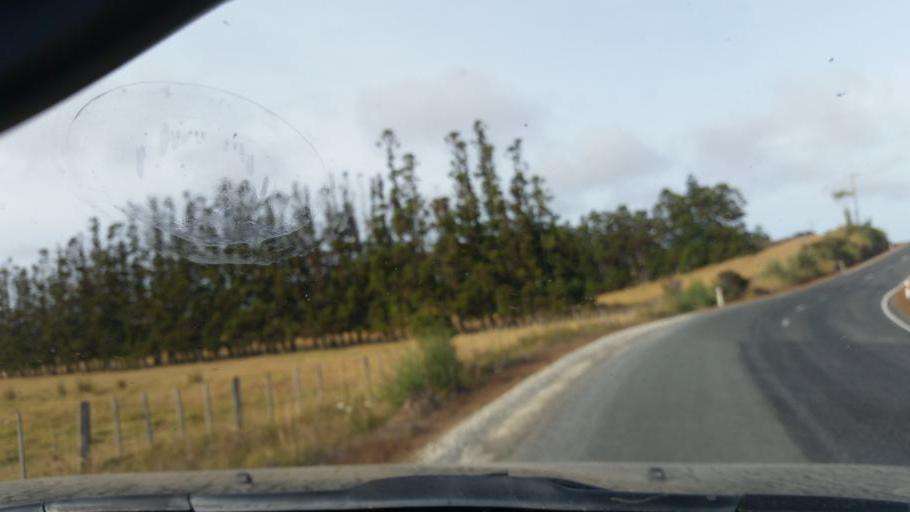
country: NZ
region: Northland
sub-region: Kaipara District
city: Dargaville
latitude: -36.2063
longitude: 174.0441
